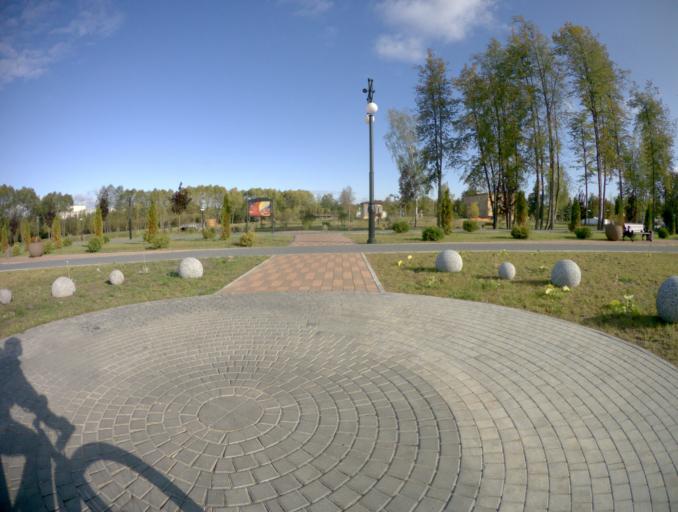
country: RU
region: Moskovskaya
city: Roshal'
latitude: 55.6609
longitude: 39.8661
